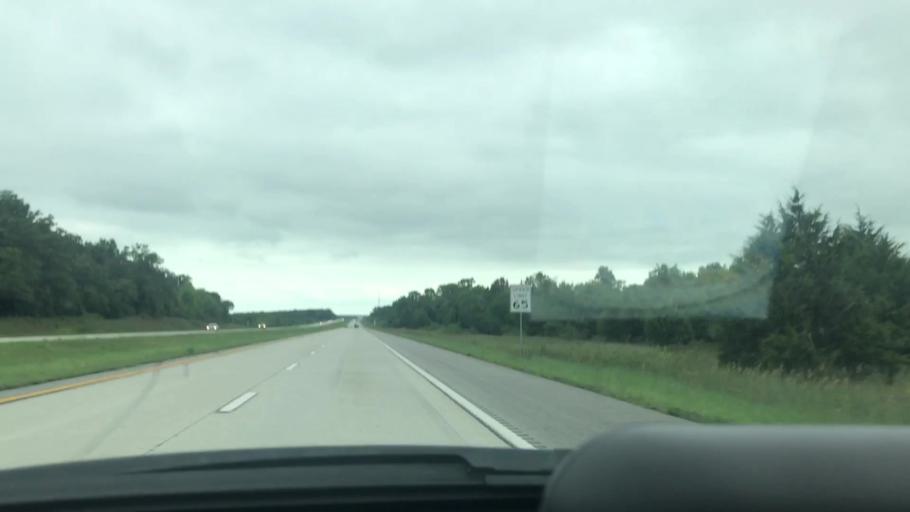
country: US
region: Missouri
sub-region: Greene County
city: Fair Grove
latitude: 37.4891
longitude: -93.1391
